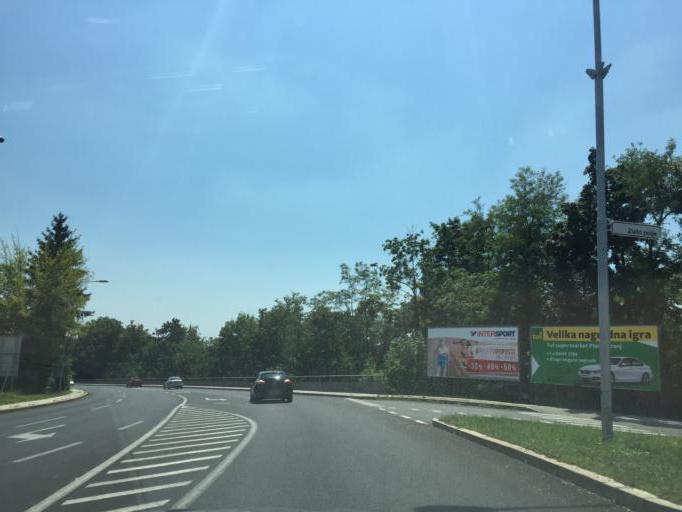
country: SI
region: Kranj
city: Kranj
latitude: 46.2474
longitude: 14.3489
